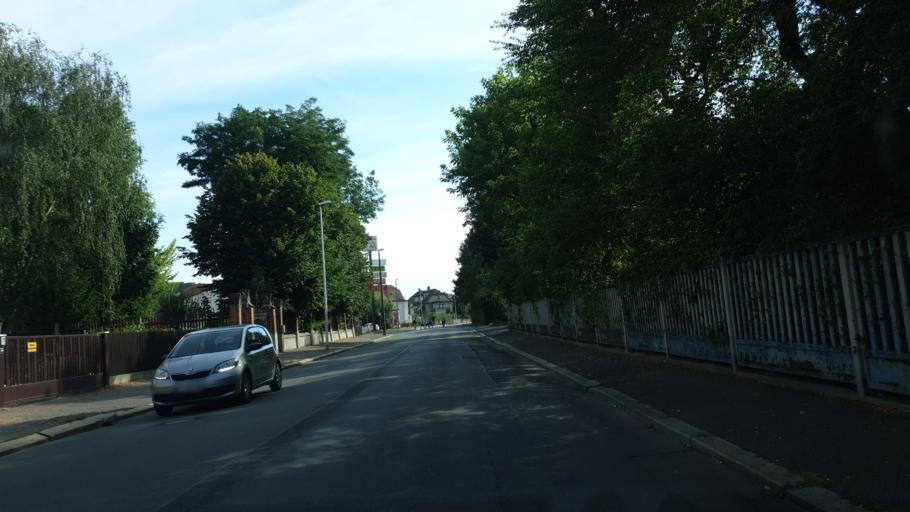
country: DE
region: Thuringia
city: Gera
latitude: 50.8461
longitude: 12.0852
